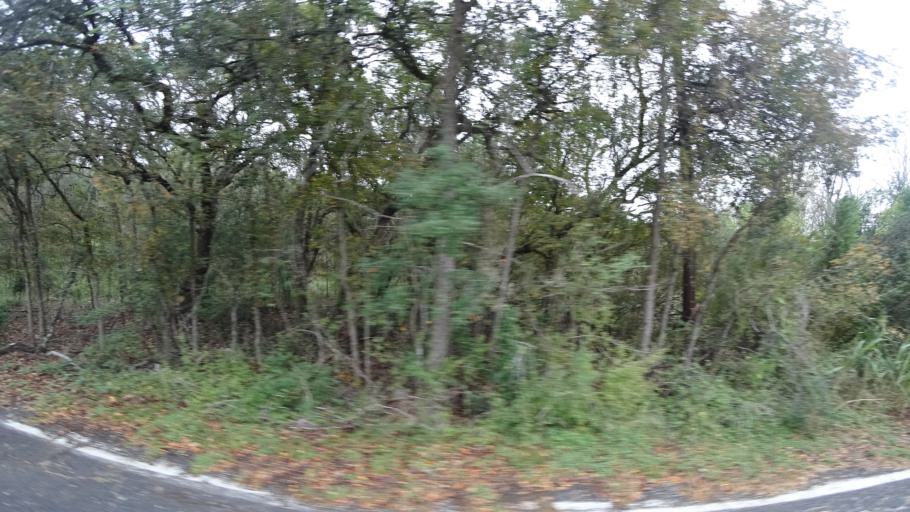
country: US
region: Texas
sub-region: Travis County
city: Barton Creek
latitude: 30.2276
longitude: -97.8995
